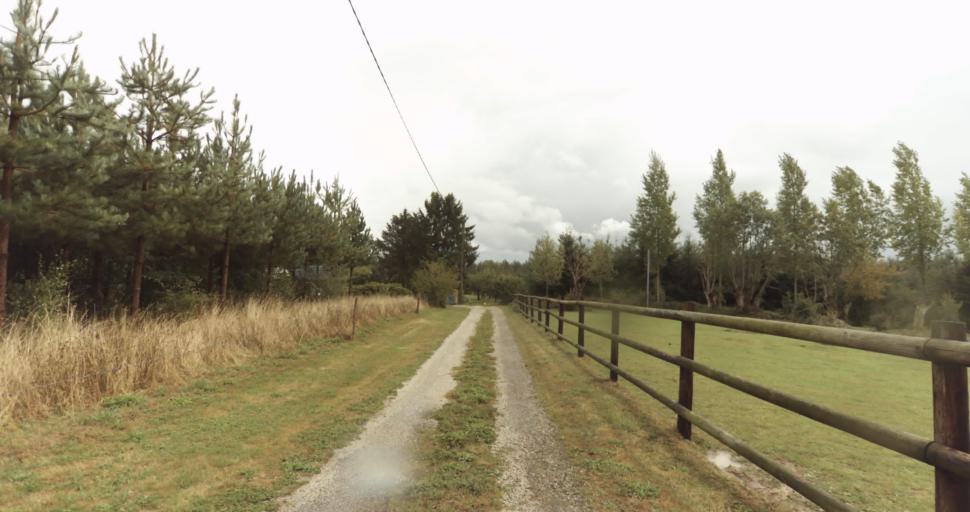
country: FR
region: Lower Normandy
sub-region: Departement de l'Orne
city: Sainte-Gauburge-Sainte-Colombe
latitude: 48.6936
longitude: 0.4174
